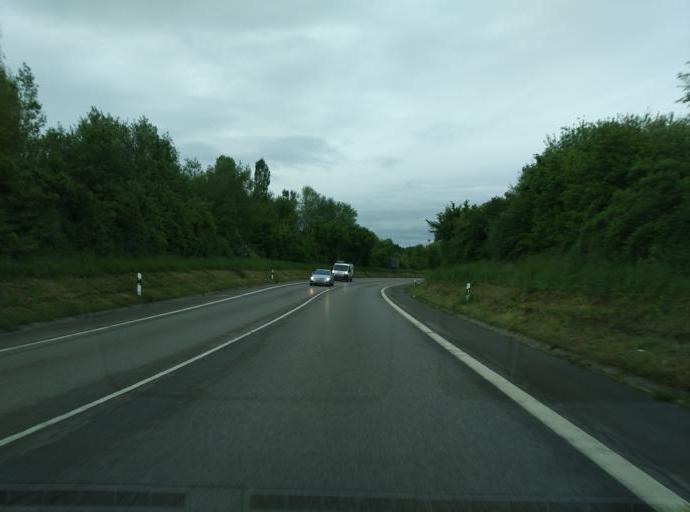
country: DE
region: Baden-Wuerttemberg
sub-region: Regierungsbezirk Stuttgart
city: Neckartailfingen
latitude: 48.6162
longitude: 9.2784
